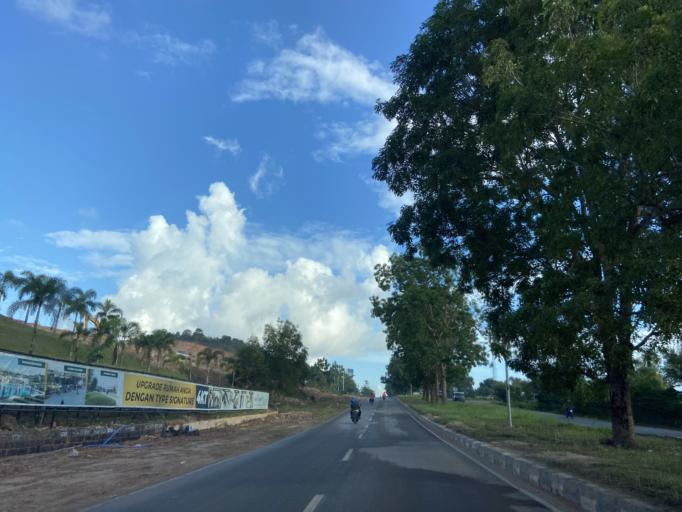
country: SG
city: Singapore
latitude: 1.0276
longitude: 104.0070
